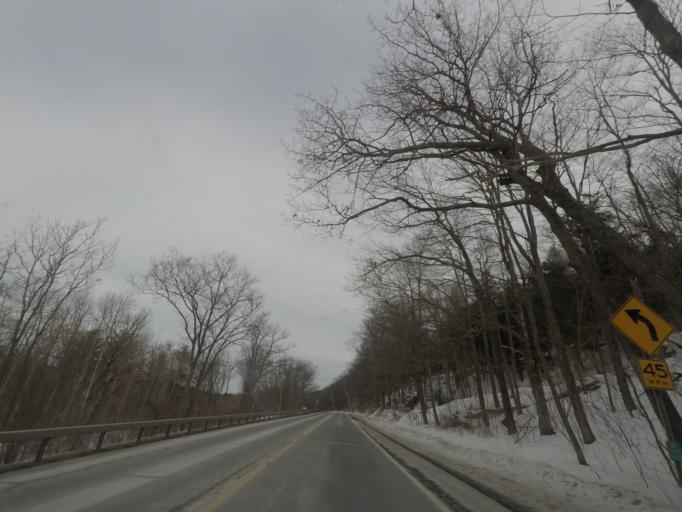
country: US
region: New York
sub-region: Albany County
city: Voorheesville
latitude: 42.5964
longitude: -74.0165
